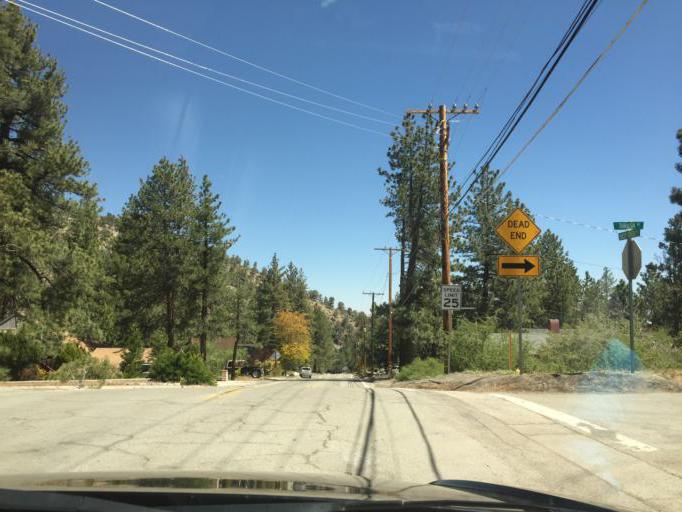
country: US
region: California
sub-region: San Bernardino County
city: Wrightwood
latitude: 34.3529
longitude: -117.6160
